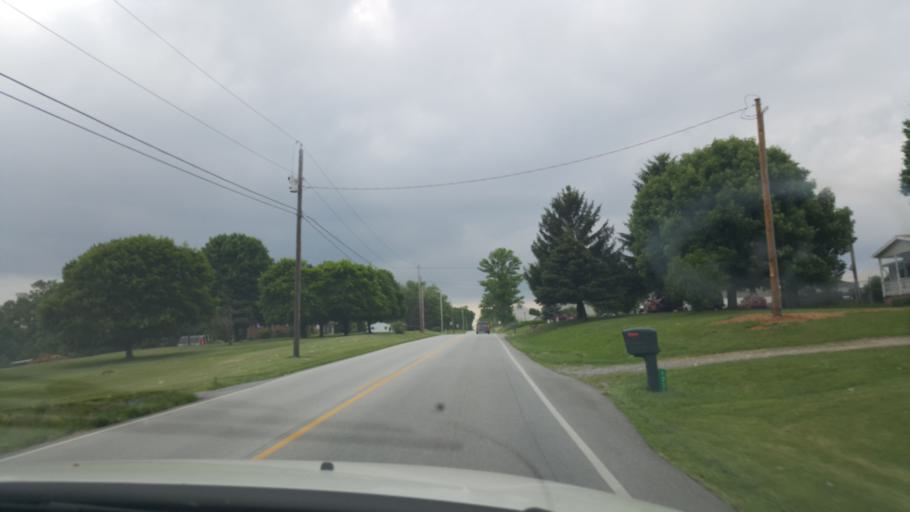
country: US
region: Pennsylvania
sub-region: Adams County
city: Lake Meade
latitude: 39.9462
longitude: -77.0916
